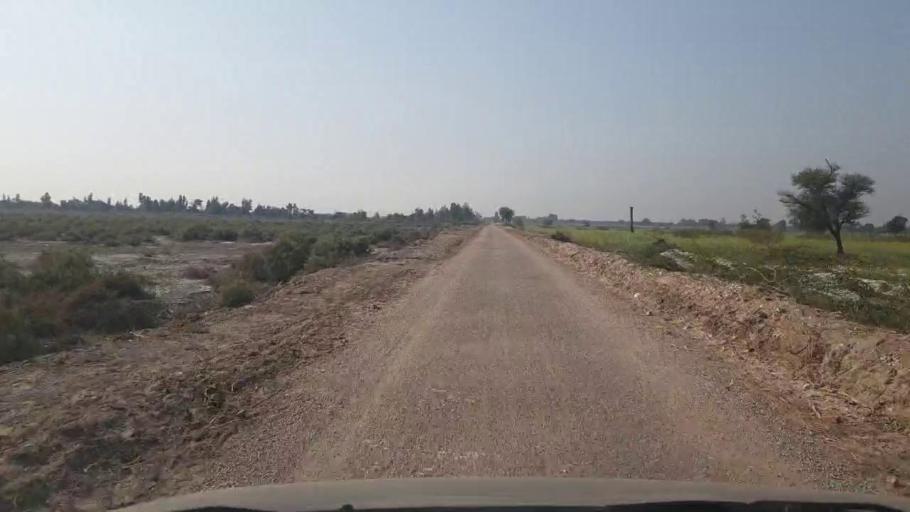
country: PK
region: Sindh
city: Mirwah Gorchani
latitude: 25.2647
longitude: 69.1149
